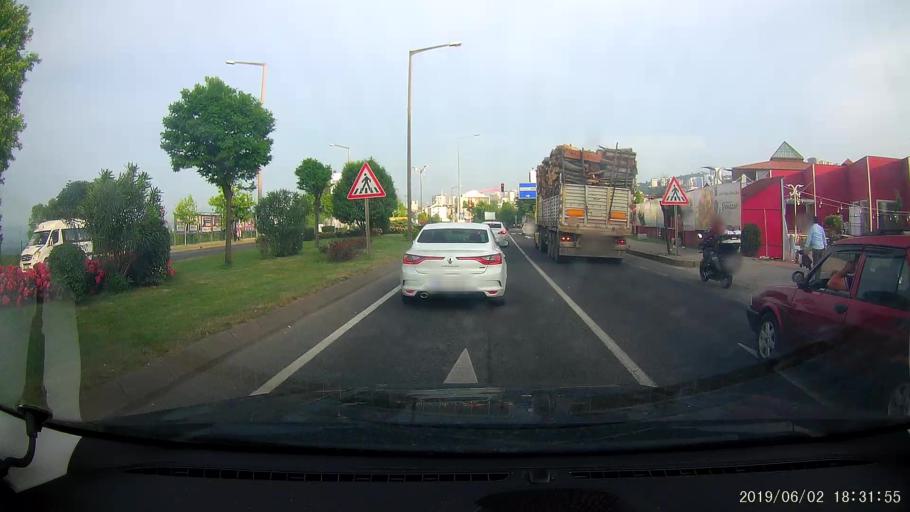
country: TR
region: Ordu
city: Fatsa
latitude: 41.0362
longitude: 37.4936
